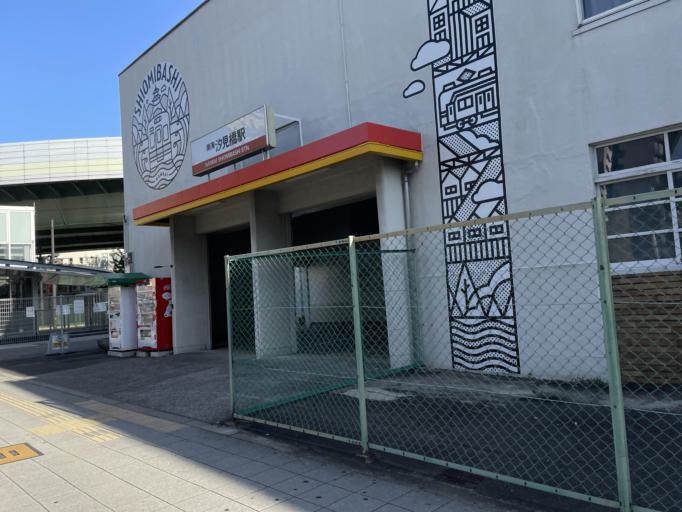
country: JP
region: Osaka
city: Osaka-shi
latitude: 34.6683
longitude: 135.4861
